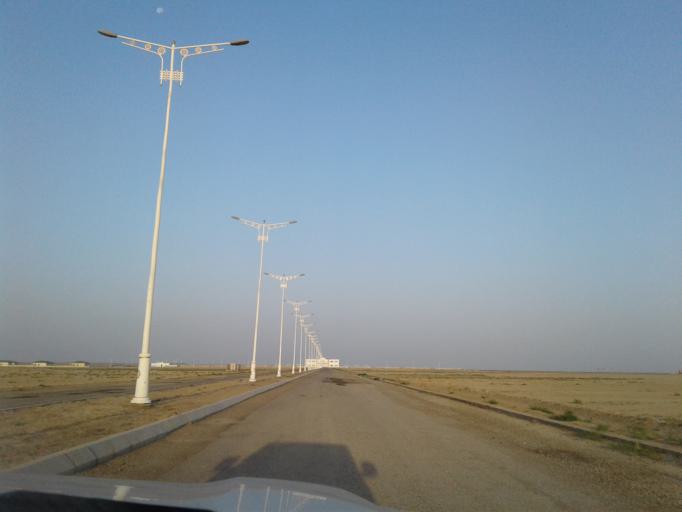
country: IR
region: Golestan
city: Aq Qayeh
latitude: 37.7063
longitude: 54.7529
